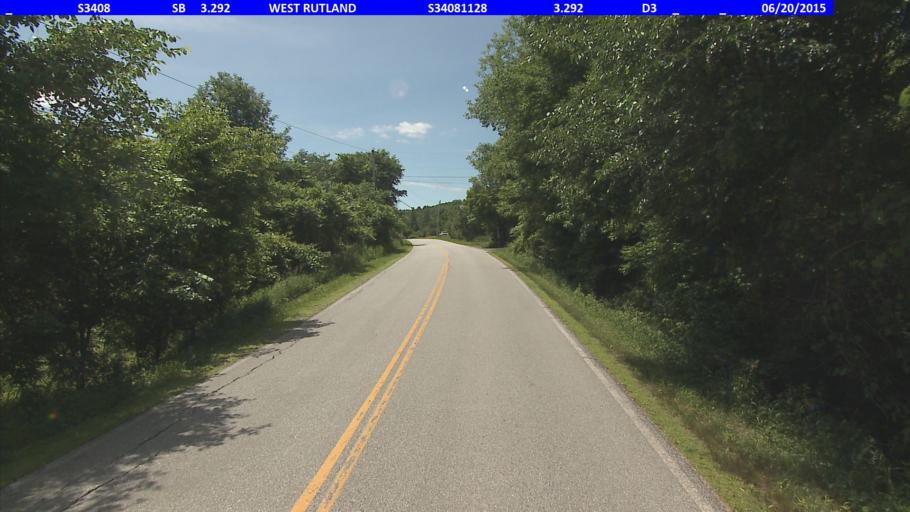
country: US
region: Vermont
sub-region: Rutland County
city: West Rutland
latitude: 43.6562
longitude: -73.0740
